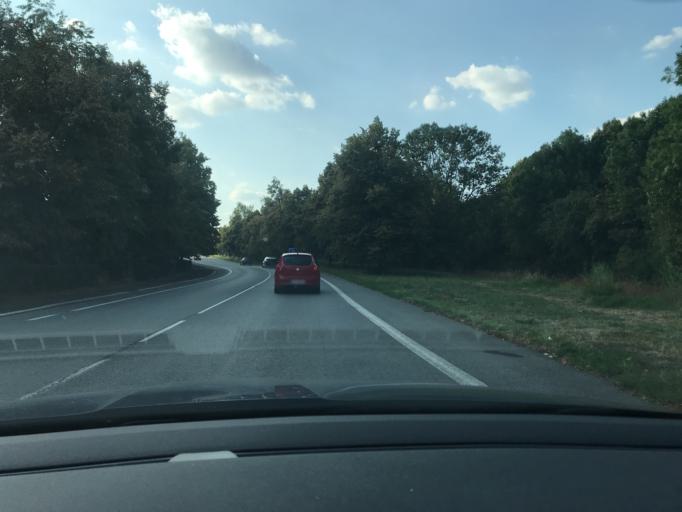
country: CZ
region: Central Bohemia
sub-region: Okres Kladno
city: Slany
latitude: 50.2341
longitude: 14.0778
